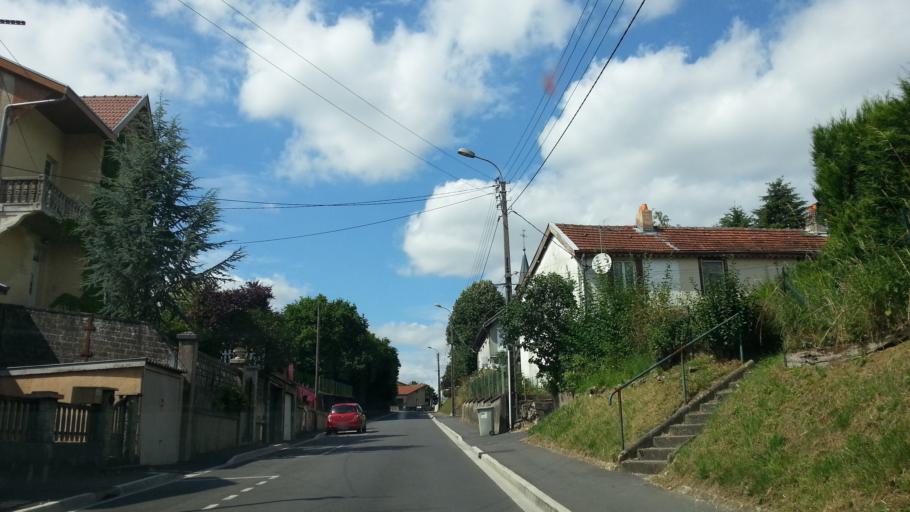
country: FR
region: Lorraine
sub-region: Departement de la Meuse
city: Thierville-sur-Meuse
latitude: 49.1594
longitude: 5.3638
